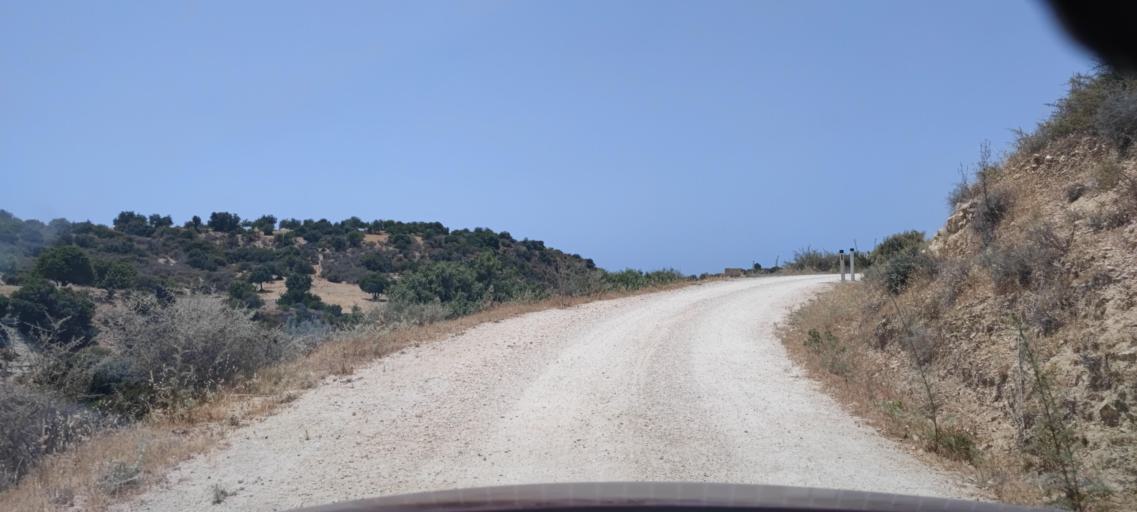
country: CY
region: Limassol
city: Pissouri
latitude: 34.7282
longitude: 32.5945
